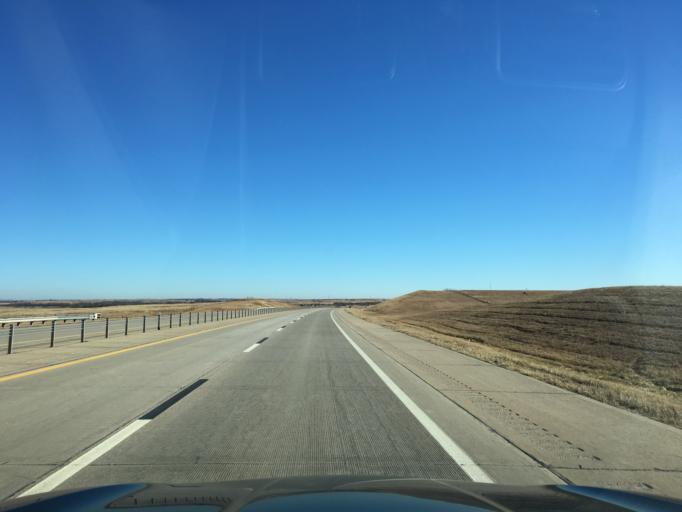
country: US
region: Oklahoma
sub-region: Noble County
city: Perry
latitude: 36.3915
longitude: -97.1037
